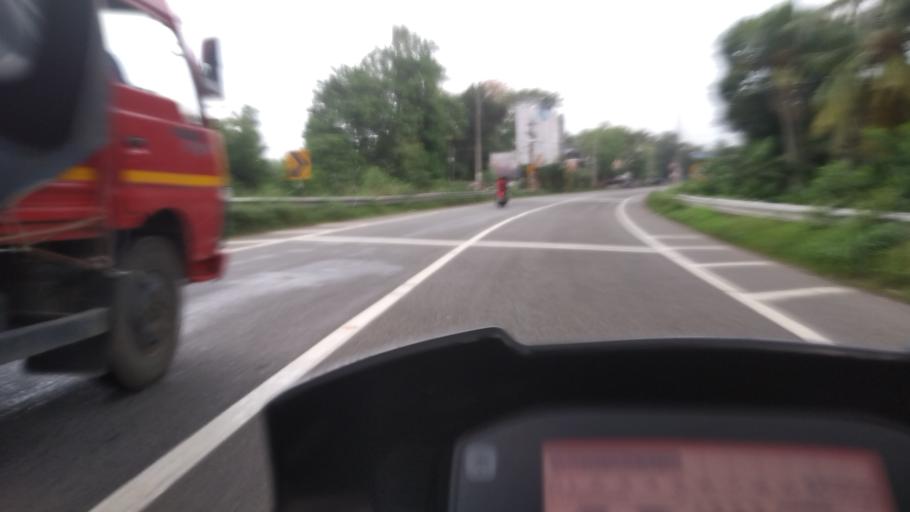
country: IN
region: Kerala
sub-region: Thiruvananthapuram
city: Attingal
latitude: 8.7112
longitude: 76.8121
